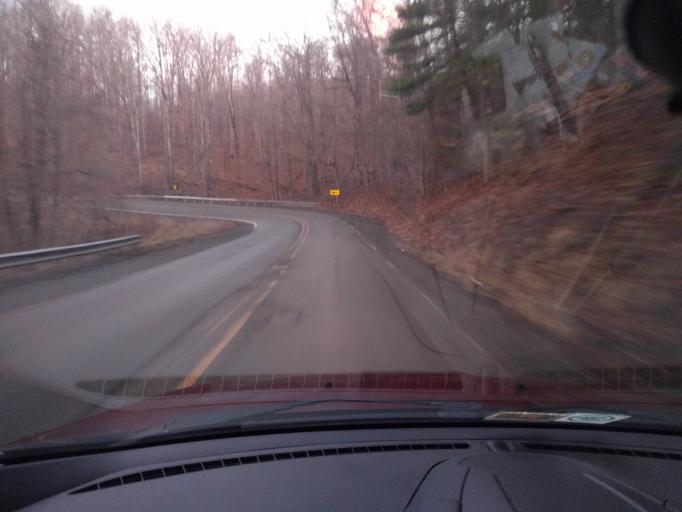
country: US
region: West Virginia
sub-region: Greenbrier County
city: Rainelle
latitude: 37.9965
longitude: -80.8678
